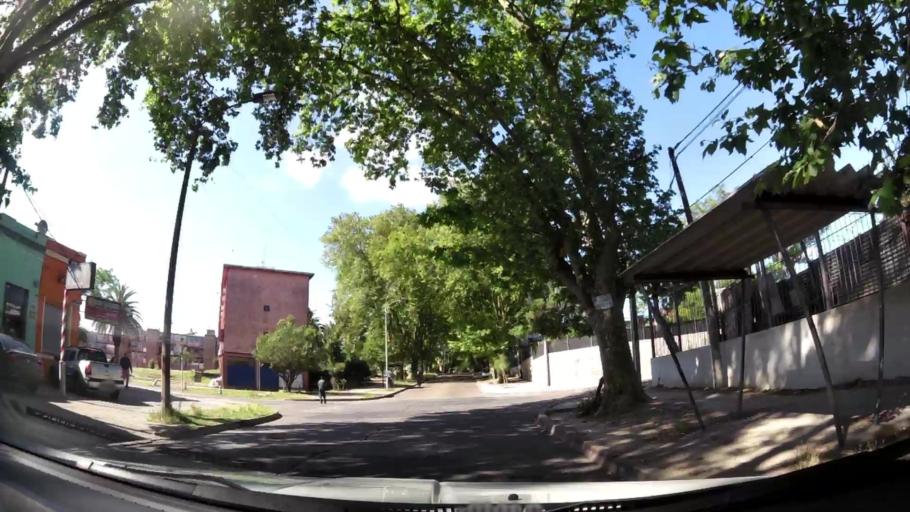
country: UY
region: Montevideo
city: Montevideo
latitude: -34.8448
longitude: -56.2113
